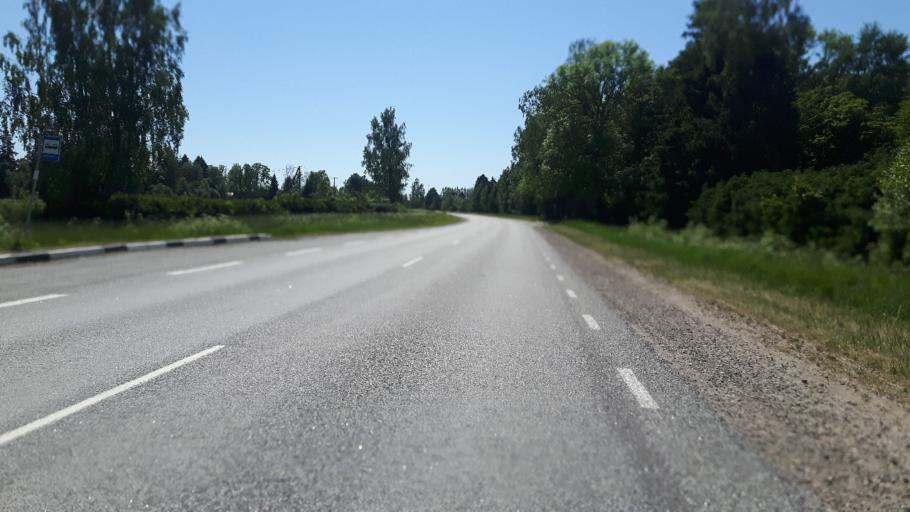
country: EE
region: Paernumaa
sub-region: Tootsi vald
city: Tootsi
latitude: 58.4664
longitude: 24.7865
